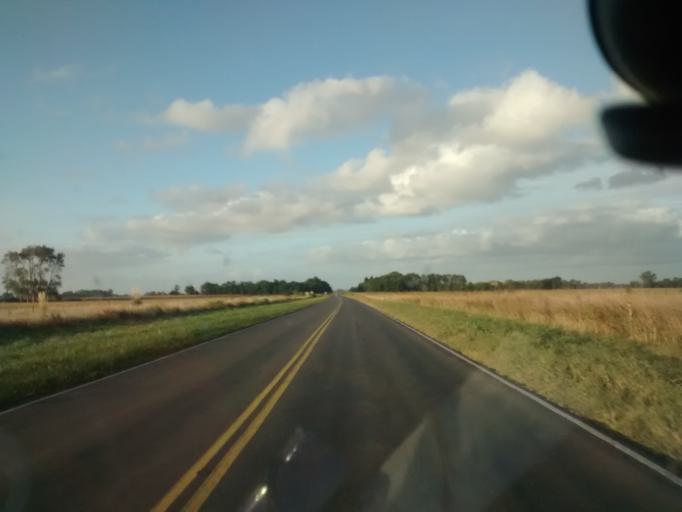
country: AR
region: Buenos Aires
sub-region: Partido de General Belgrano
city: General Belgrano
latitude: -35.8050
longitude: -58.5590
